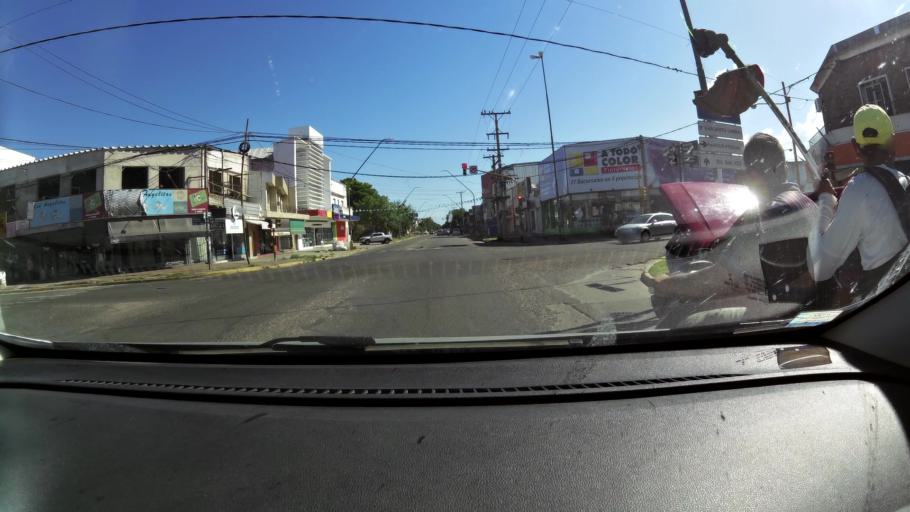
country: AR
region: Santa Fe
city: Santa Fe de la Vera Cruz
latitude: -31.6204
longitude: -60.6860
